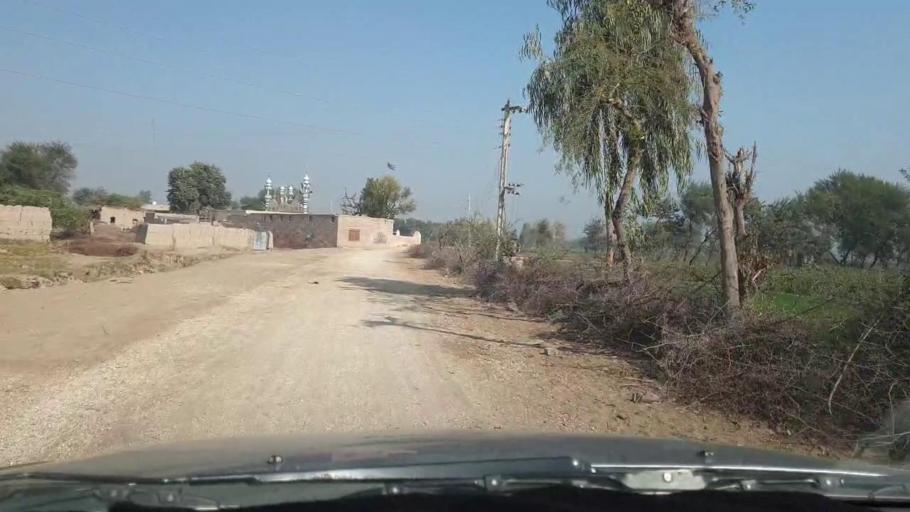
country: PK
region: Sindh
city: Khanpur
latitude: 27.8082
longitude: 69.5616
